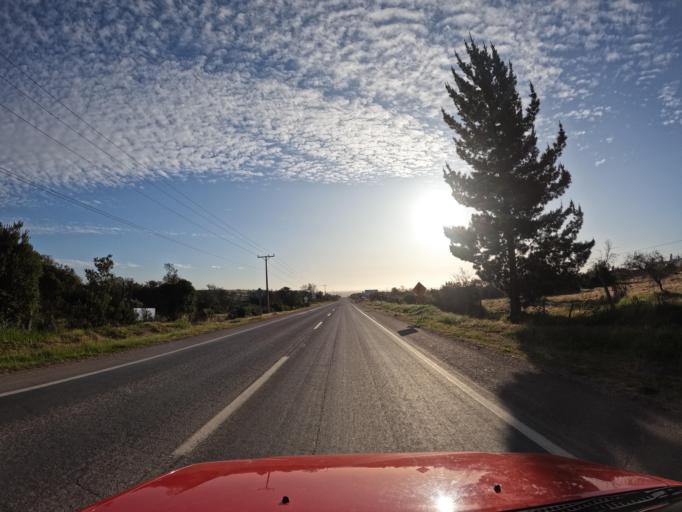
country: CL
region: Valparaiso
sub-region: San Antonio Province
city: San Antonio
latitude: -34.0856
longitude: -71.6698
